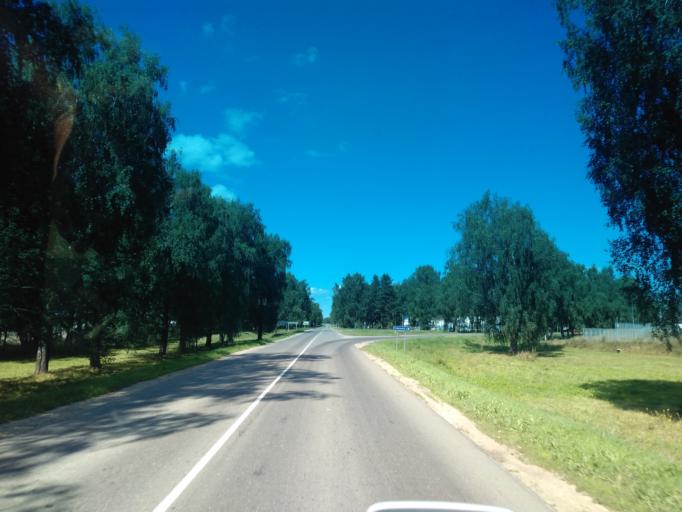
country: BY
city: Fanipol
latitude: 53.7231
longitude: 27.3380
